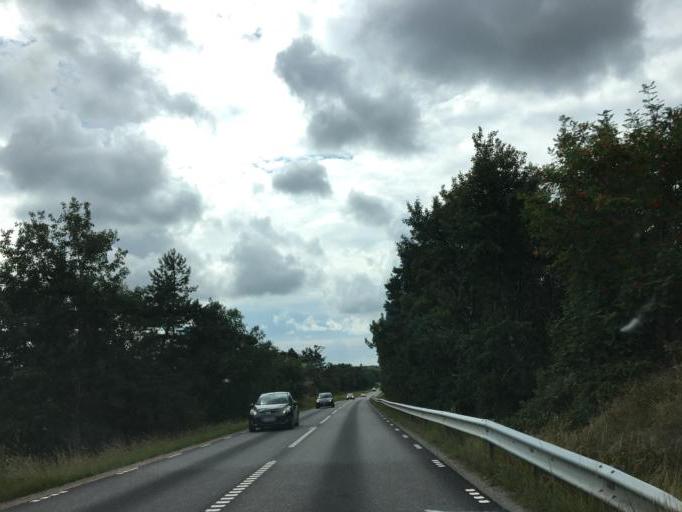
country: SE
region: Vaestra Goetaland
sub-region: Sotenas Kommun
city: Hunnebostrand
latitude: 58.4094
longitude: 11.2740
